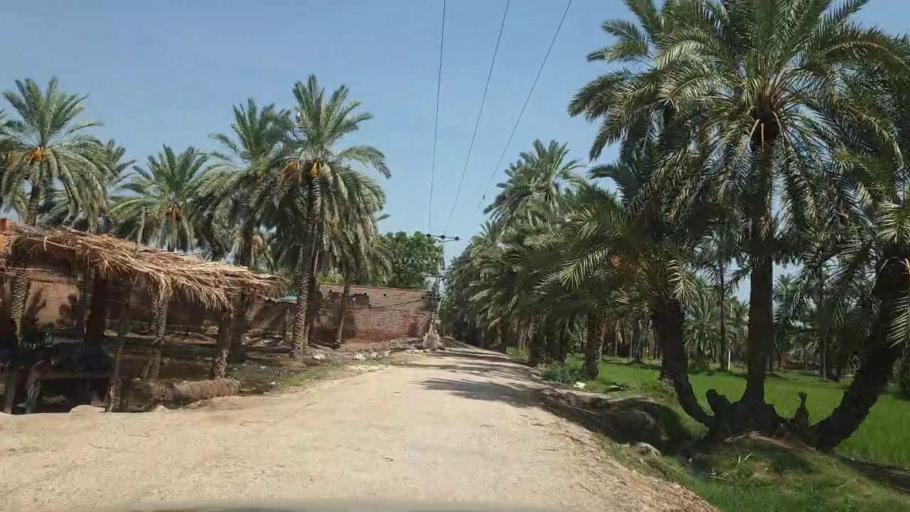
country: PK
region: Sindh
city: Rohri
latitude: 27.6930
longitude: 68.9477
